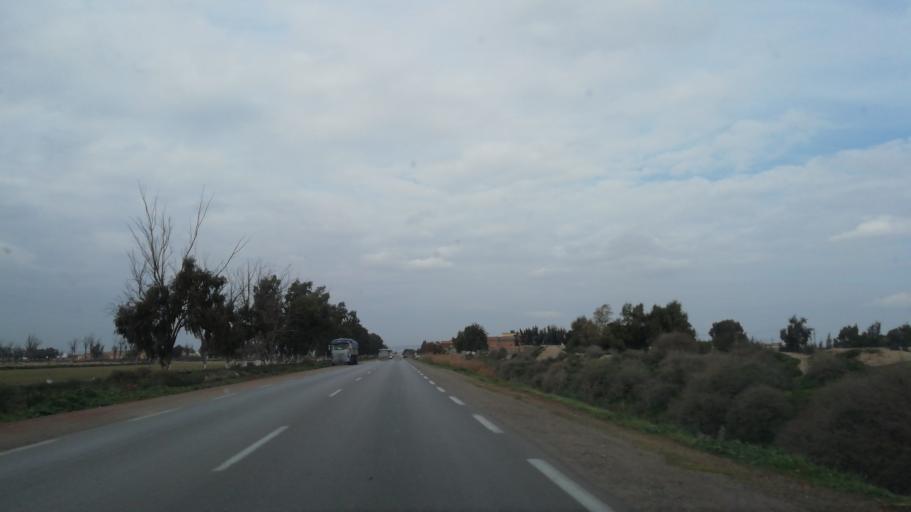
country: DZ
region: Mostaganem
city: Mostaganem
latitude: 35.6811
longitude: 0.0569
